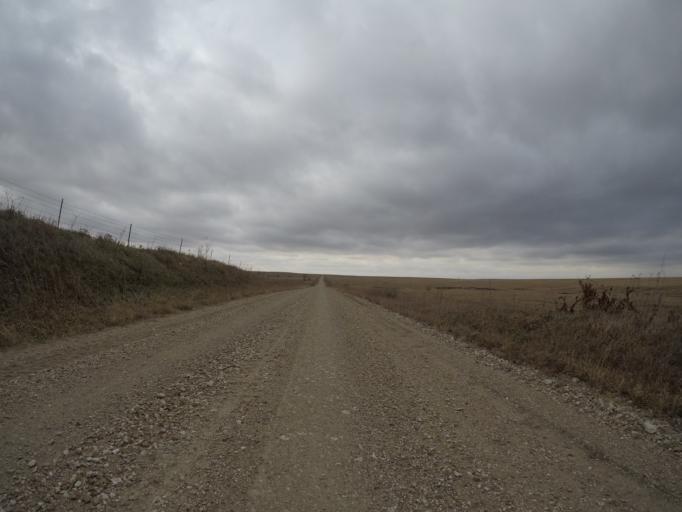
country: US
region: Kansas
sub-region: Wabaunsee County
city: Alma
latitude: 38.7245
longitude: -96.1800
